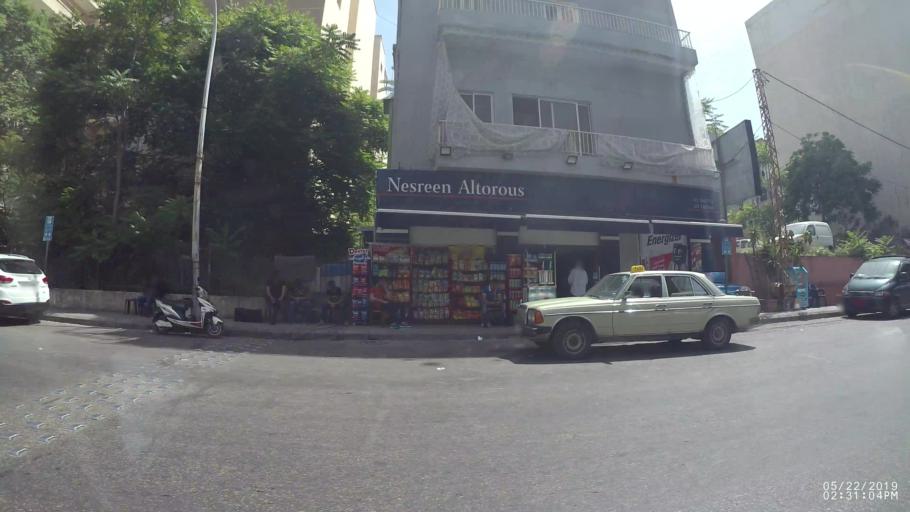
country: LB
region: Beyrouth
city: Ra's Bayrut
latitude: 33.9012
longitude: 35.4922
